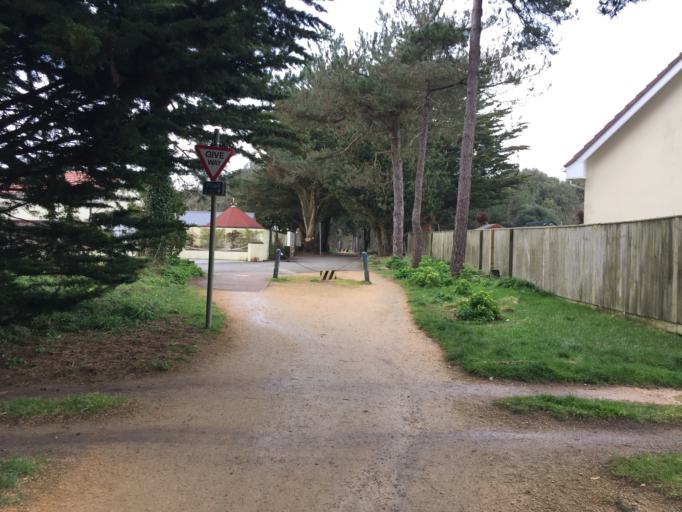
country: JE
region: St Helier
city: Saint Helier
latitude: 49.1890
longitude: -2.2170
